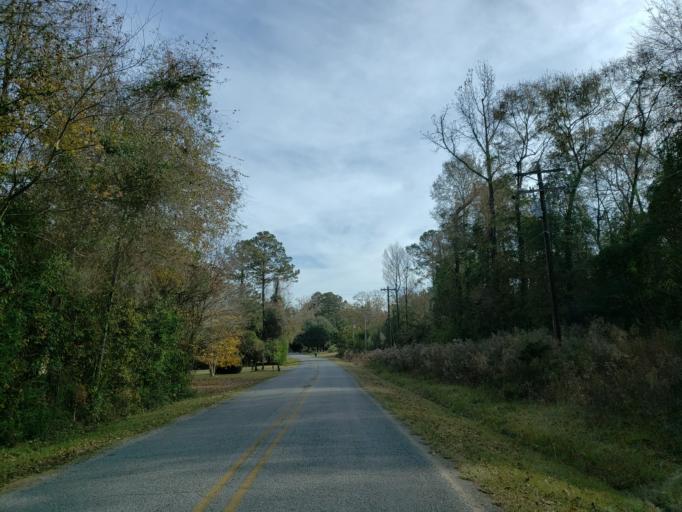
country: US
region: Mississippi
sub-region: Forrest County
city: Rawls Springs
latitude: 31.3735
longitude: -89.3646
